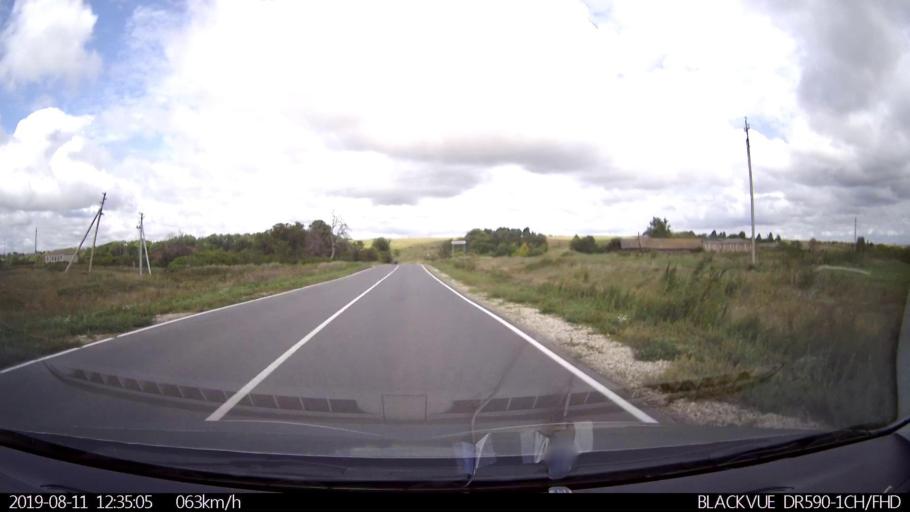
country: RU
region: Ulyanovsk
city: Ignatovka
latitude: 53.8216
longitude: 47.8348
